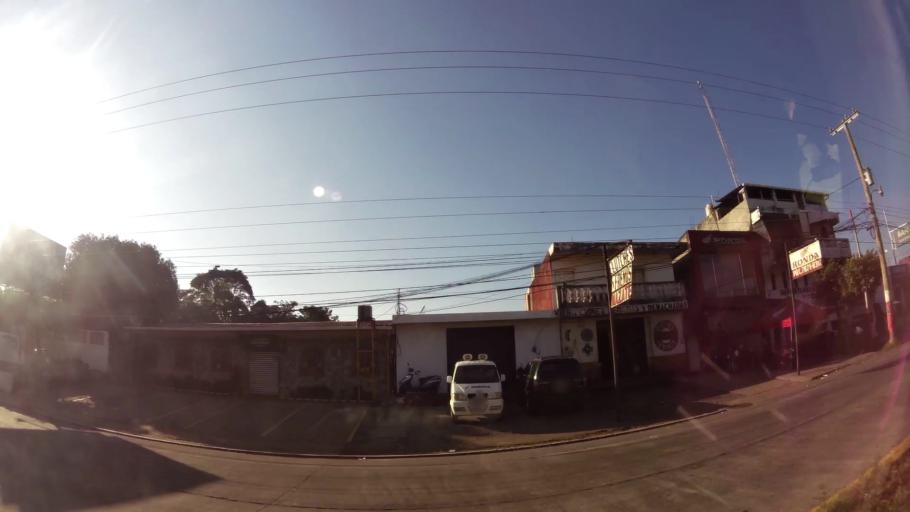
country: GT
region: Suchitepeque
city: Mazatenango
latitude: 14.5331
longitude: -91.5139
